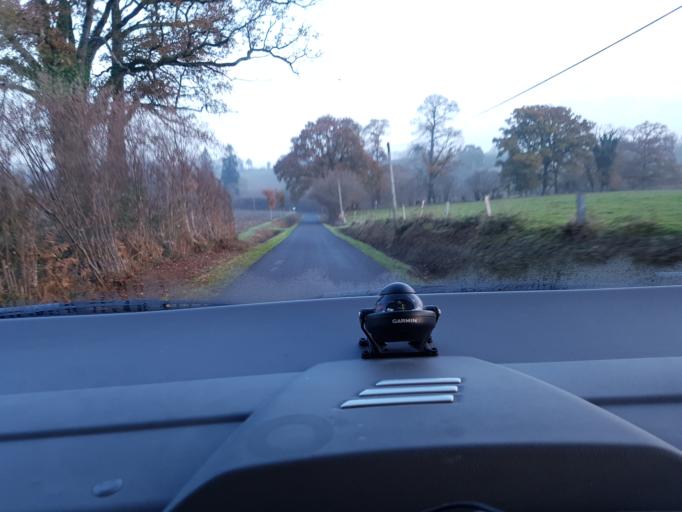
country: FR
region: Lower Normandy
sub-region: Departement de l'Orne
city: Champsecret
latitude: 48.6339
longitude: -0.5810
